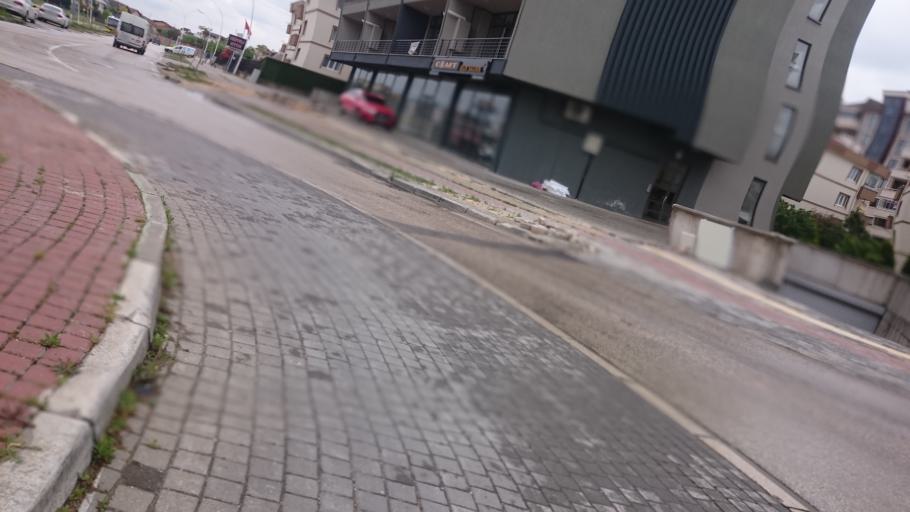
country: TR
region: Bursa
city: Cali
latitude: 40.2181
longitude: 28.9255
